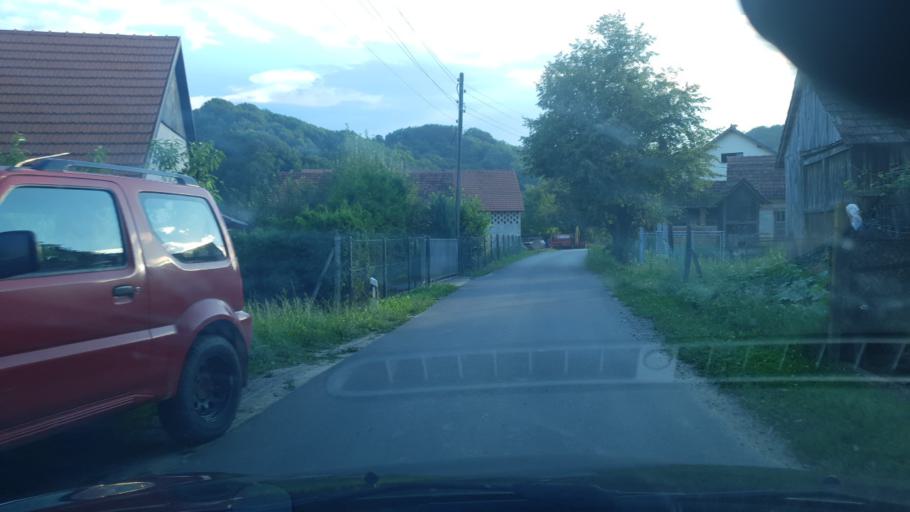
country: HR
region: Krapinsko-Zagorska
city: Zabok
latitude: 46.0833
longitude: 15.8965
